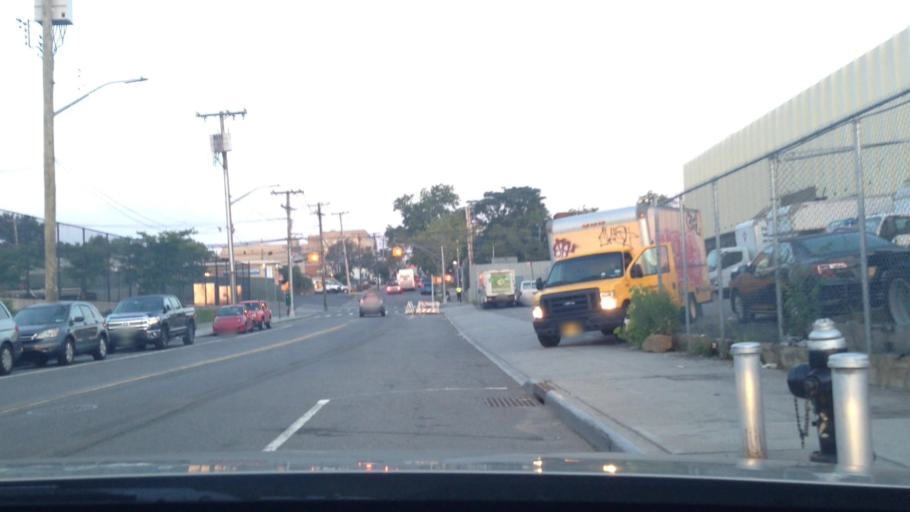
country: US
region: New York
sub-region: Bronx
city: The Bronx
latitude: 40.7787
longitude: -73.8377
